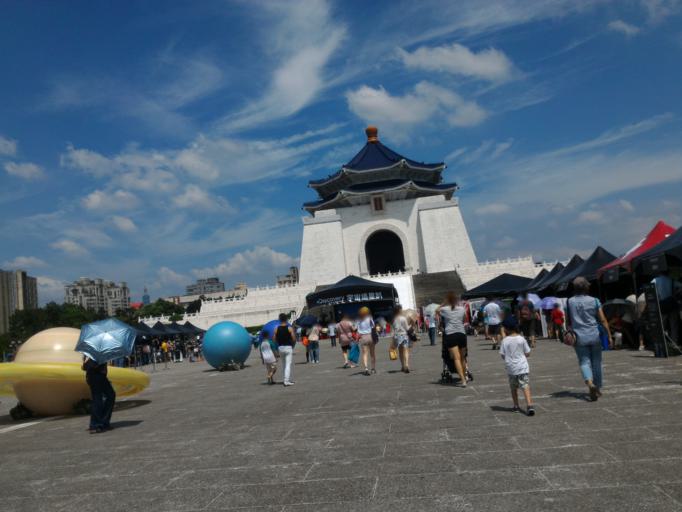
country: TW
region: Taipei
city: Taipei
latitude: 25.0354
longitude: 121.5200
